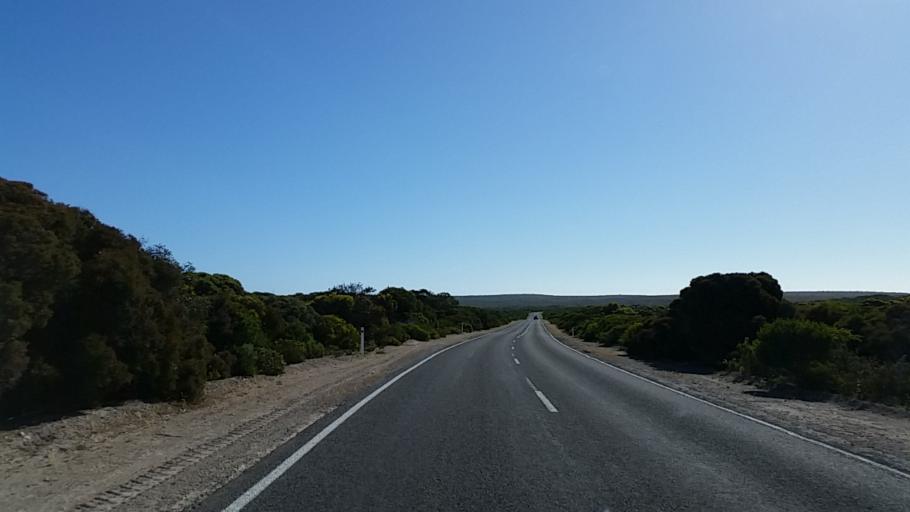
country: AU
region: South Australia
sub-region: Yorke Peninsula
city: Honiton
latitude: -35.2625
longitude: 136.9551
